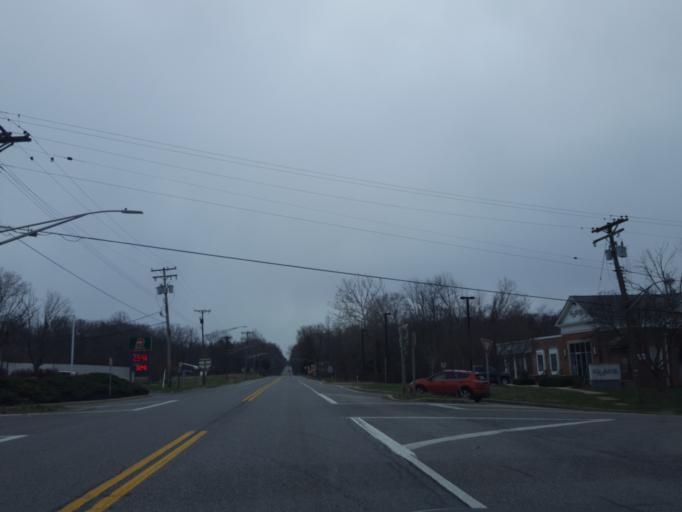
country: US
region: Maryland
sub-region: Calvert County
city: Owings
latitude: 38.7179
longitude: -76.6019
